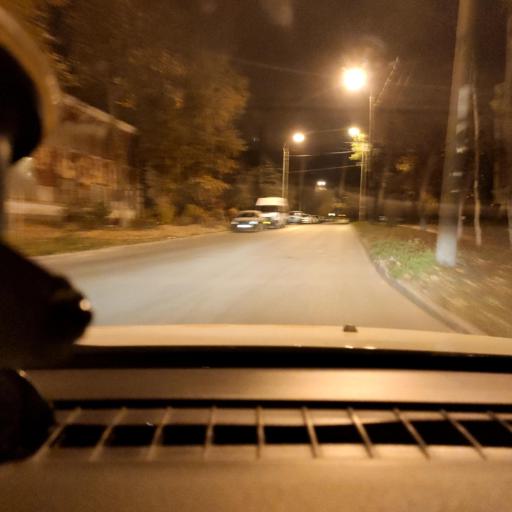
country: RU
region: Samara
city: Samara
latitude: 53.1980
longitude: 50.2193
